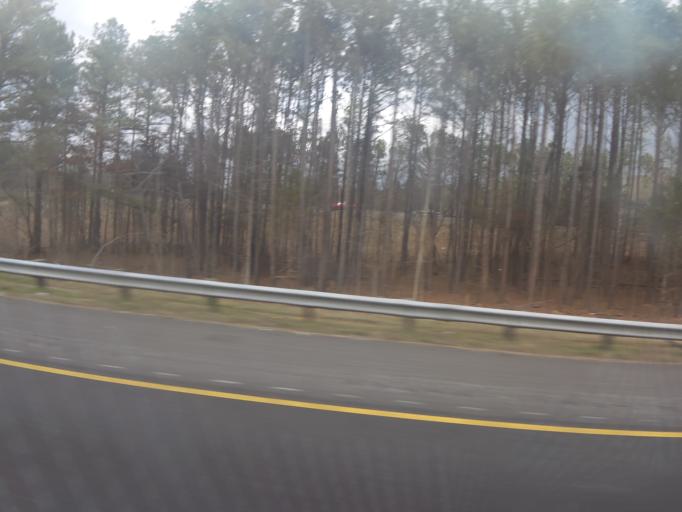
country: US
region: Georgia
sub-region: Catoosa County
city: Indian Springs
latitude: 34.9402
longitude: -85.1667
